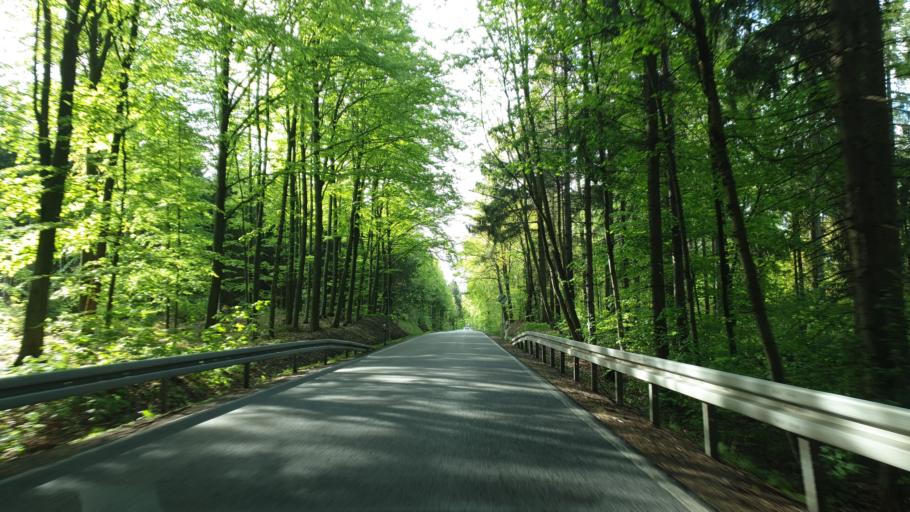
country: DE
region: Saxony
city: Lichtenstein
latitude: 50.7190
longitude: 12.6512
